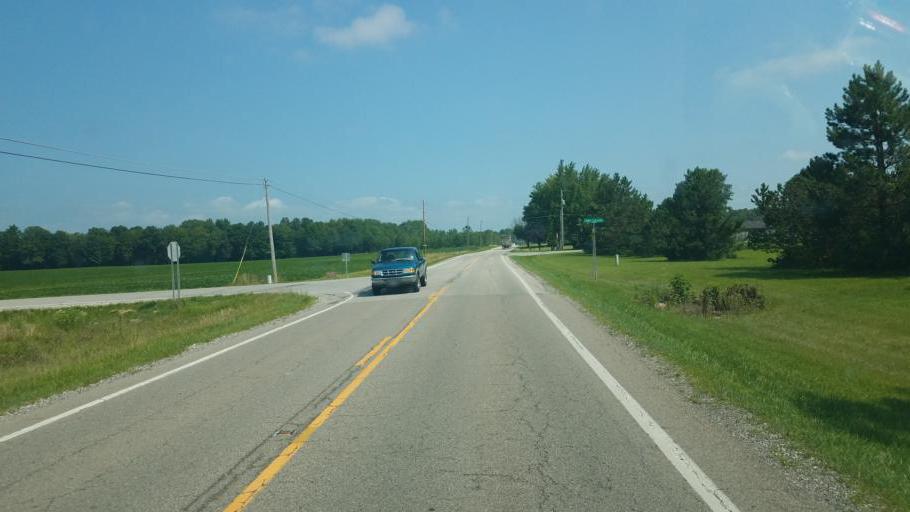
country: US
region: Ohio
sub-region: Crawford County
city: Galion
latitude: 40.7984
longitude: -82.8570
